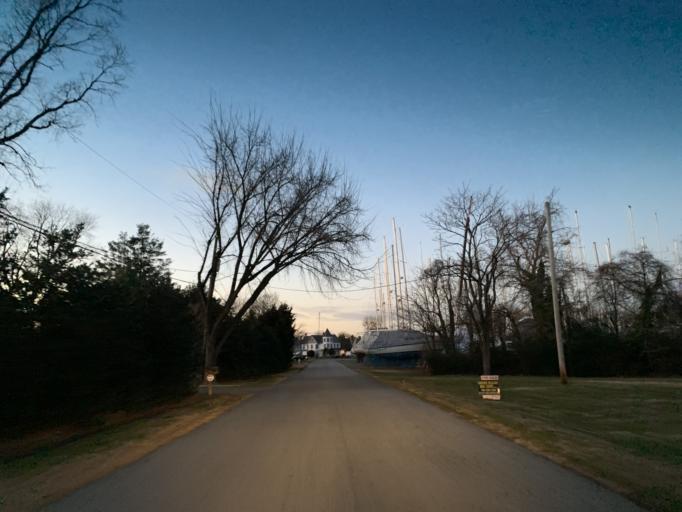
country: US
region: Maryland
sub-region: Kent County
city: Rock Hall
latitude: 39.1397
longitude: -76.2587
